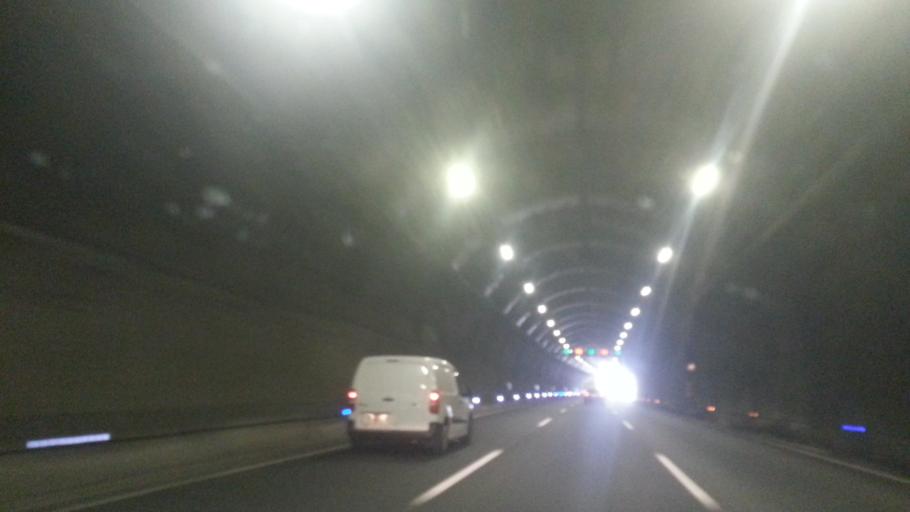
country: ES
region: Catalonia
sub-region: Provincia de Barcelona
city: Castelloli
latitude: 41.5955
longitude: 1.7402
